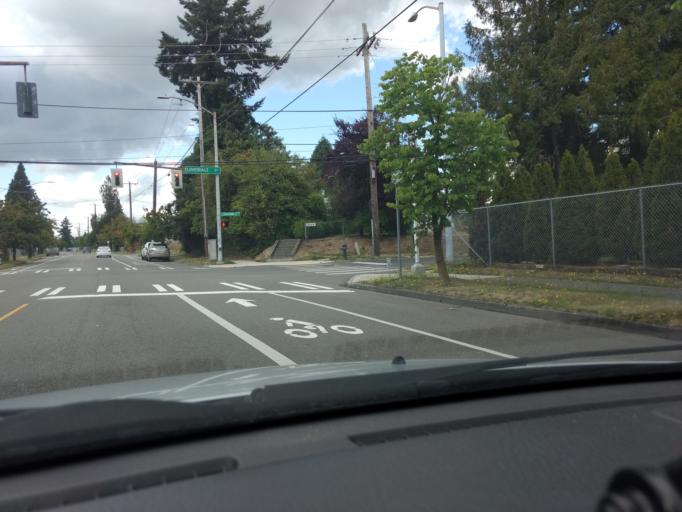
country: US
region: Washington
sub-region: King County
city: Riverton
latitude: 47.5259
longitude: -122.2769
